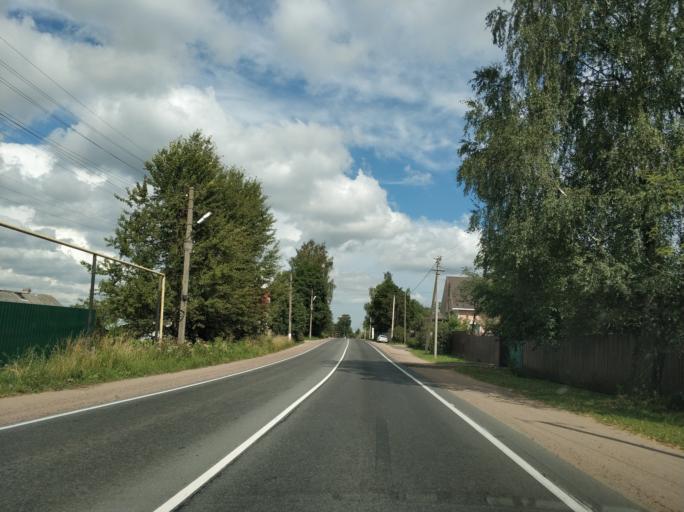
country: RU
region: Leningrad
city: Romanovka
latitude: 60.0505
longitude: 30.7227
